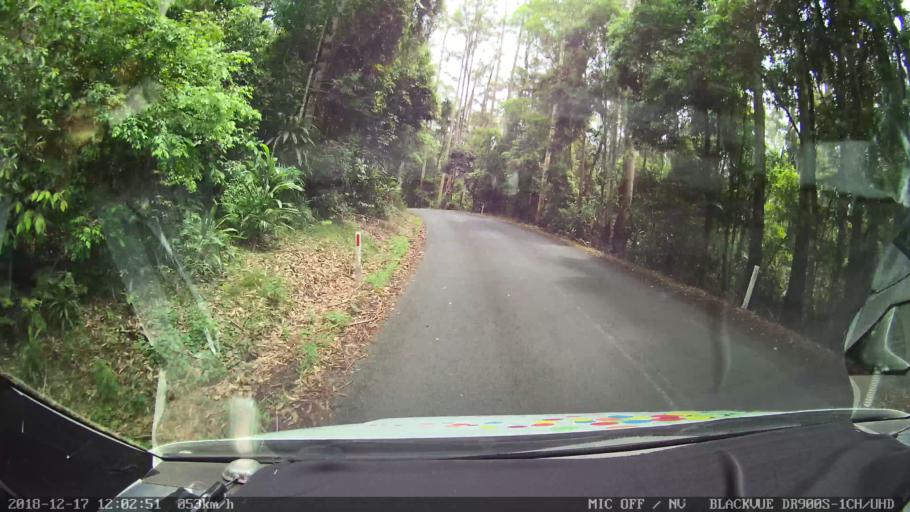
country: AU
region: New South Wales
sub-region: Kyogle
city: Kyogle
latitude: -28.5128
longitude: 152.5696
